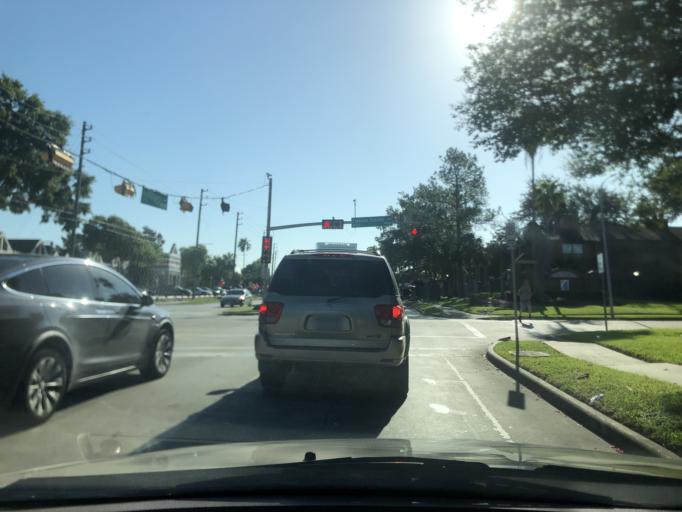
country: US
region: Texas
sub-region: Harris County
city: Bunker Hill Village
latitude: 29.7476
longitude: -95.5699
